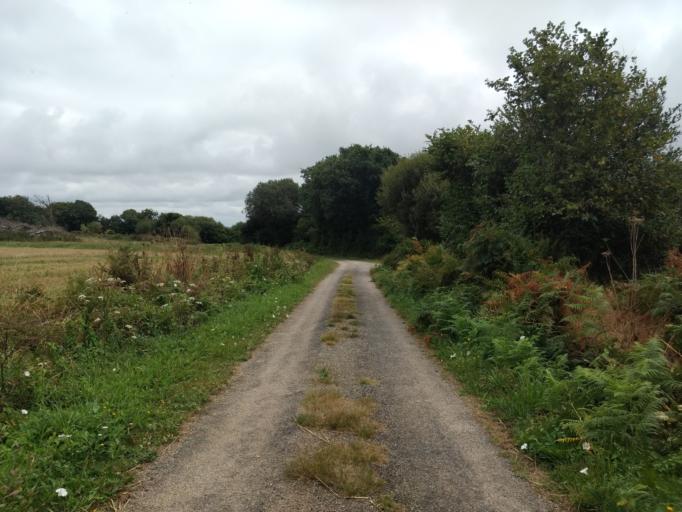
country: FR
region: Brittany
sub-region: Departement du Finistere
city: Loperhet
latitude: 48.3673
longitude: -4.2923
